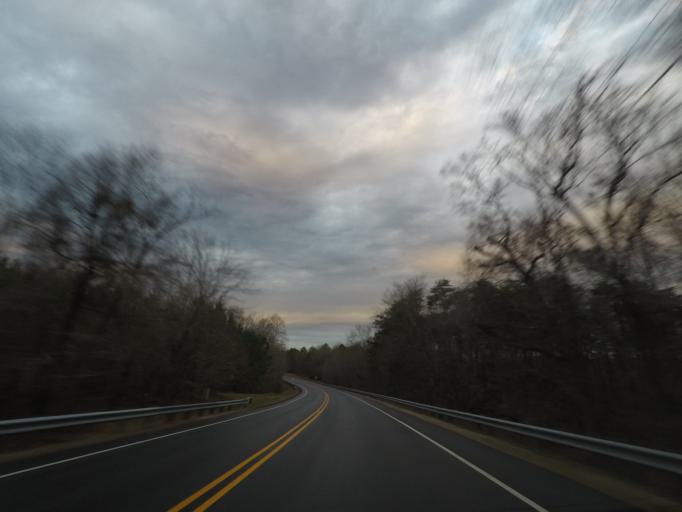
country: US
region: North Carolina
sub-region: Caswell County
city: Yanceyville
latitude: 36.4083
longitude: -79.3245
